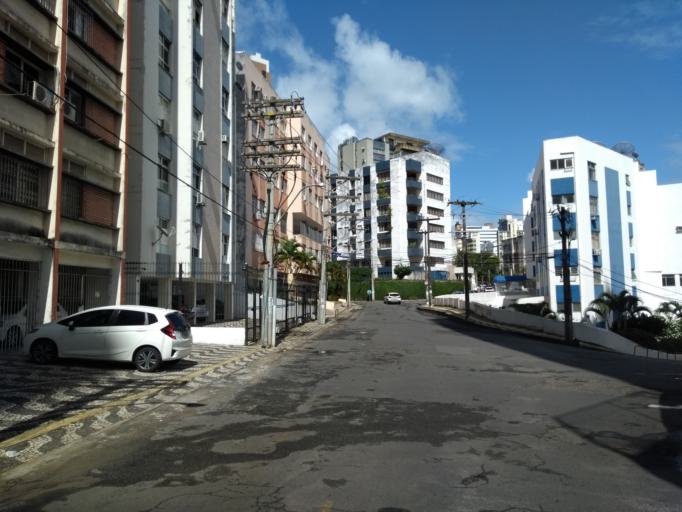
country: BR
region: Bahia
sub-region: Salvador
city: Salvador
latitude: -13.0038
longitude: -38.5203
